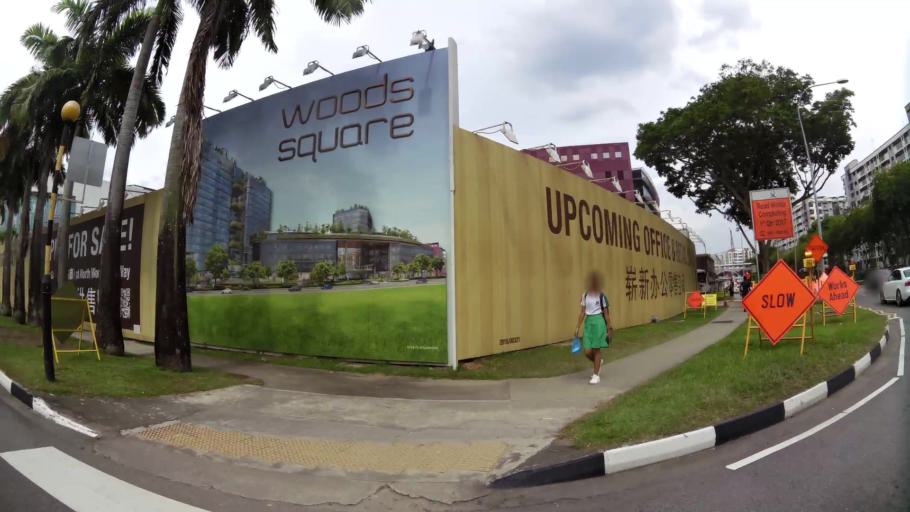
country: MY
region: Johor
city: Johor Bahru
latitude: 1.4345
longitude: 103.7857
